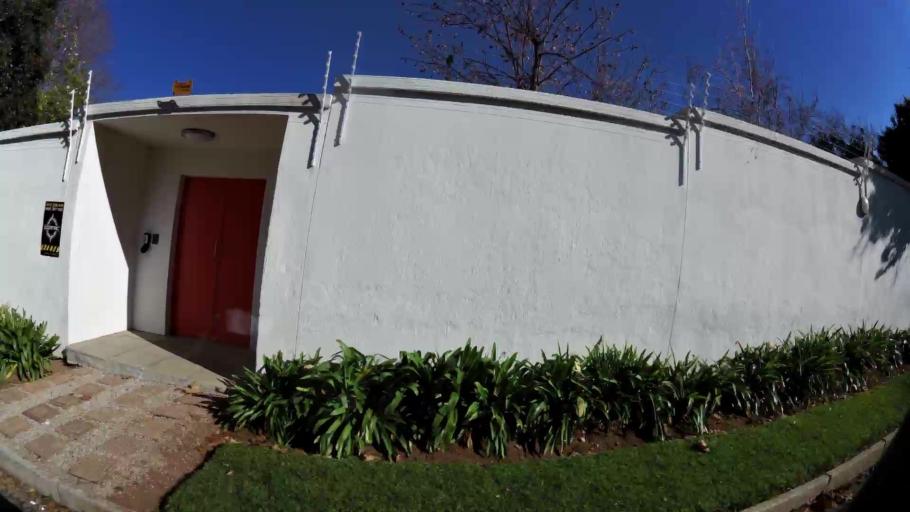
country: ZA
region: Gauteng
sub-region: City of Johannesburg Metropolitan Municipality
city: Johannesburg
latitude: -26.1474
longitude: 28.0220
